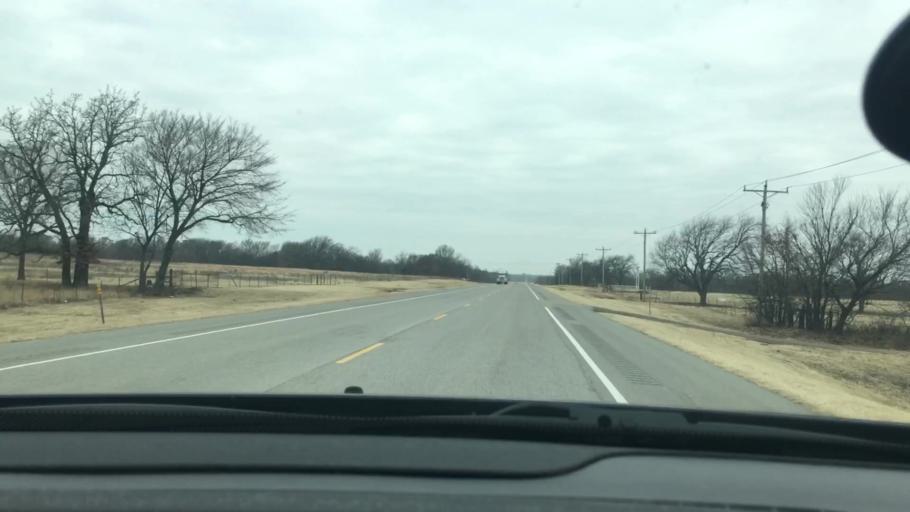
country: US
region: Oklahoma
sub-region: Carter County
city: Healdton
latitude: 34.4924
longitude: -97.4217
